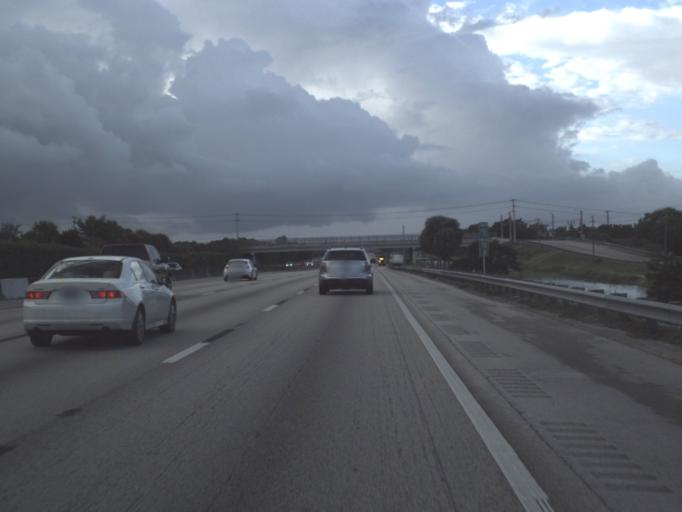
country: US
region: Florida
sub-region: Palm Beach County
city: Boca Pointe
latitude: 26.3347
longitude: -80.1705
